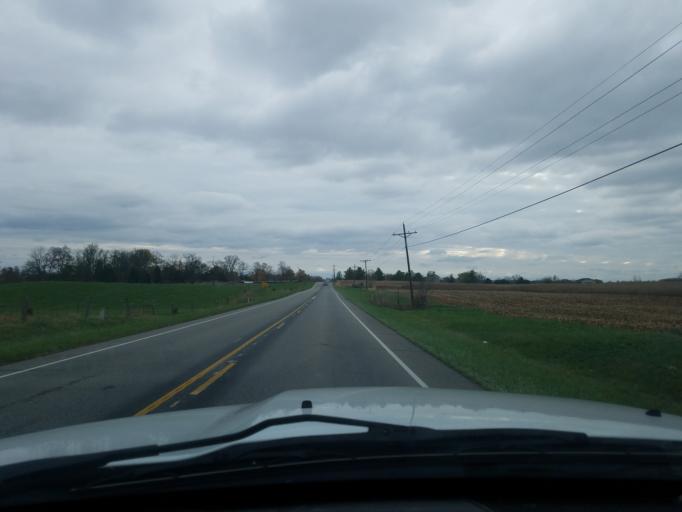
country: US
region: Indiana
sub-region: Bartholomew County
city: Hope
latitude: 39.2437
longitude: -85.7717
